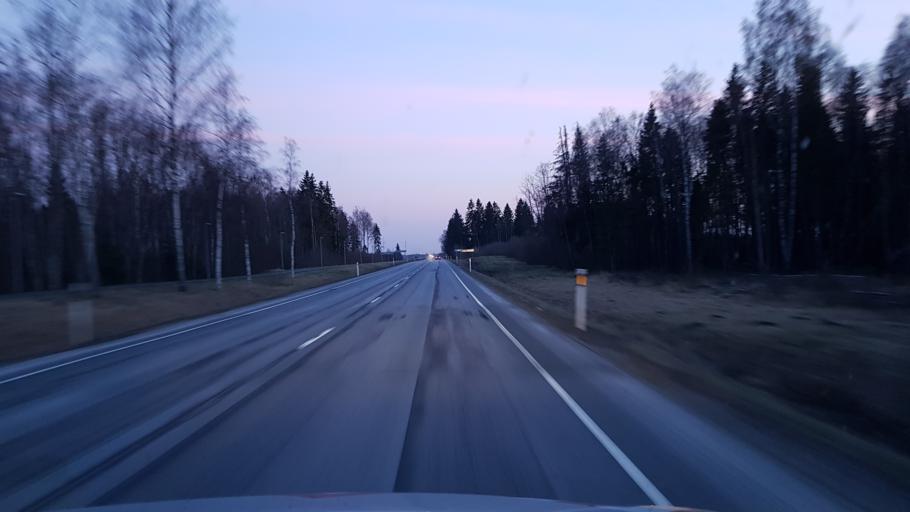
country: EE
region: Jaervamaa
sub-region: Paide linn
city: Paide
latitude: 58.9294
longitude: 25.6300
